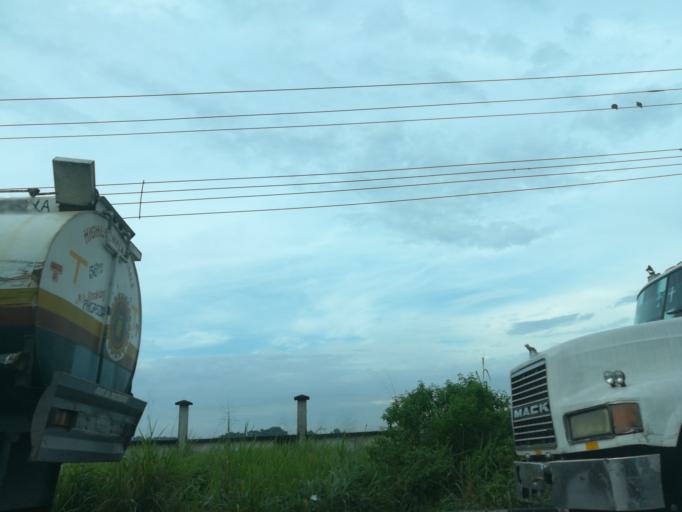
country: NG
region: Rivers
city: Port Harcourt
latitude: 4.7828
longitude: 7.0050
